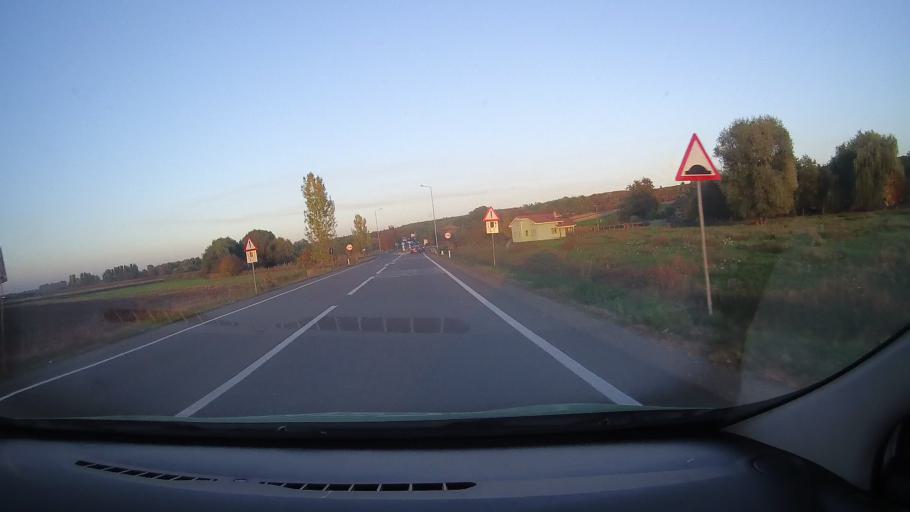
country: RO
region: Bihor
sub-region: Comuna Sacueni
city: Cadea
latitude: 47.3301
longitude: 22.0812
